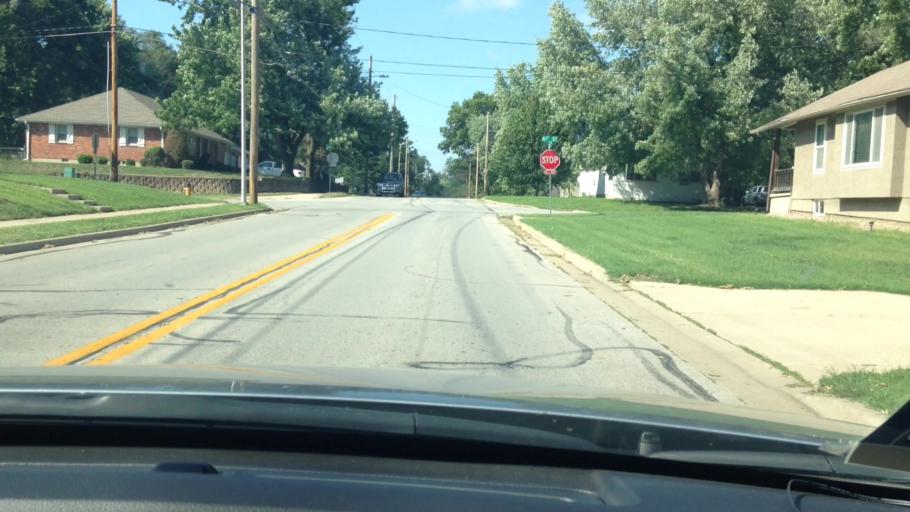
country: US
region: Kansas
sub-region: Johnson County
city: Shawnee
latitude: 39.0179
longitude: -94.7309
